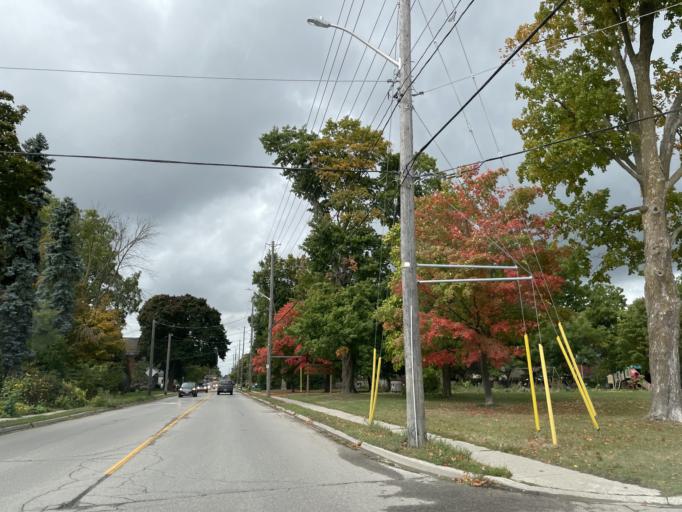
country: CA
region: Ontario
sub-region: Wellington County
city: Guelph
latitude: 43.5384
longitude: -80.2593
